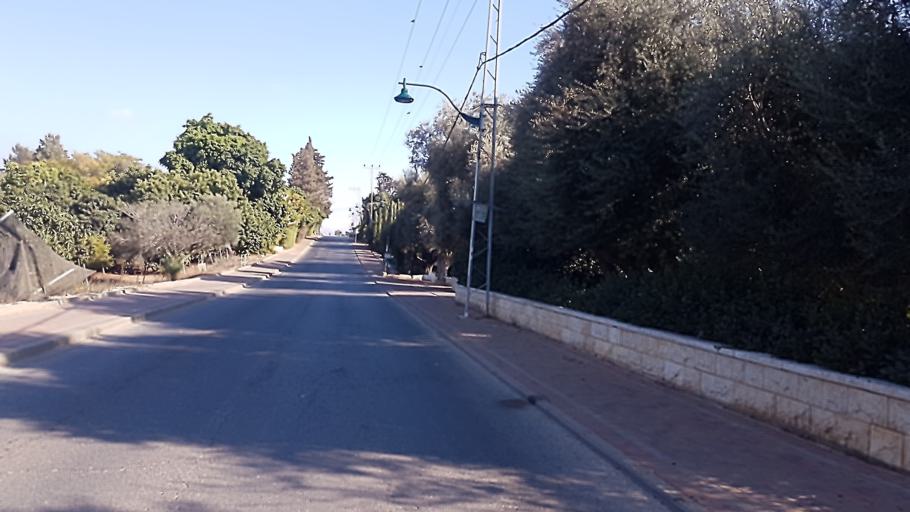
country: IL
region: Central District
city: Kfar Saba
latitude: 32.2014
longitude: 34.9137
